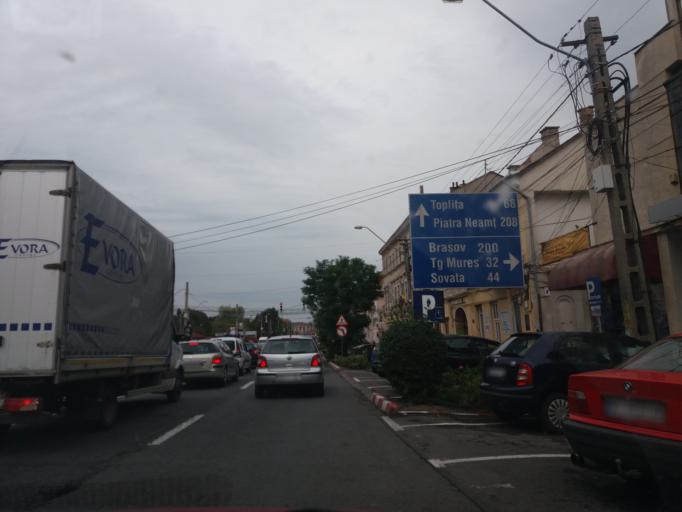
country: RO
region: Mures
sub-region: Municipiul Reghin
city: Reghin
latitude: 46.7790
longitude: 24.6998
